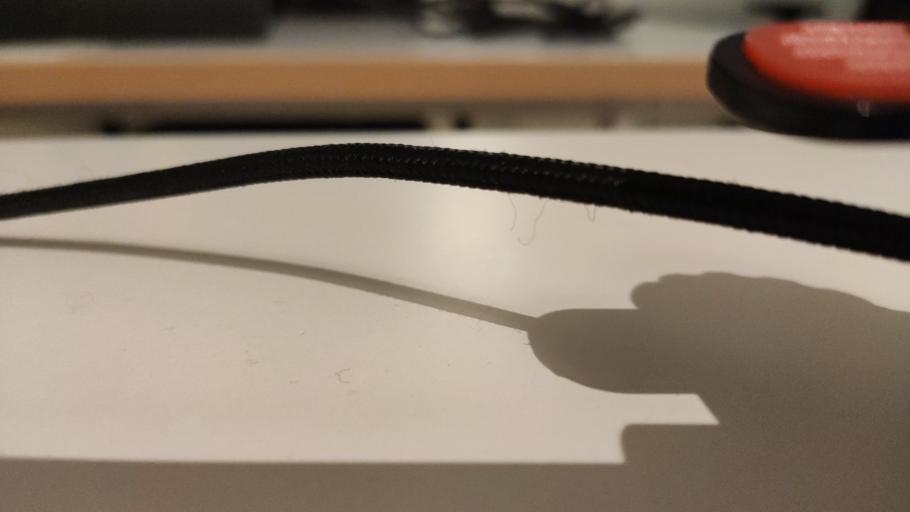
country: RU
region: Moskovskaya
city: Novosin'kovo
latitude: 56.3711
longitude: 37.3478
